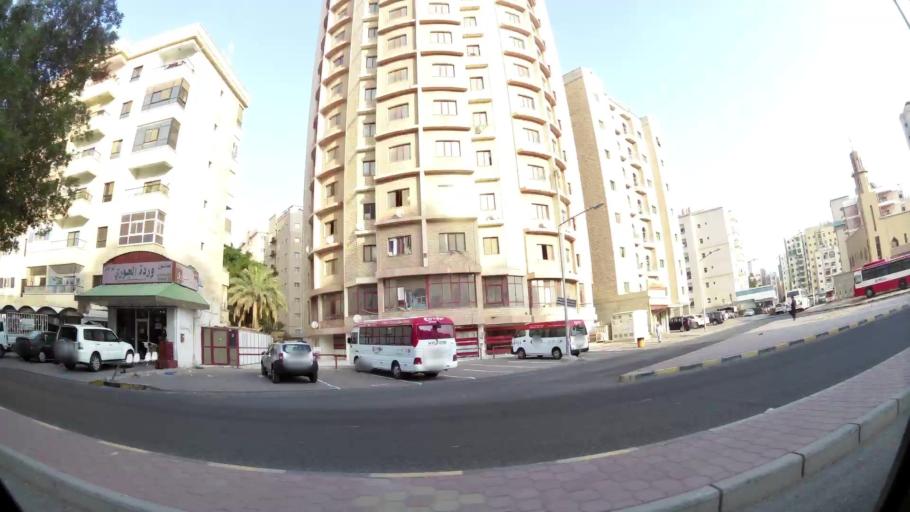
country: KW
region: Muhafazat Hawalli
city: As Salimiyah
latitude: 29.3297
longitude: 48.0674
